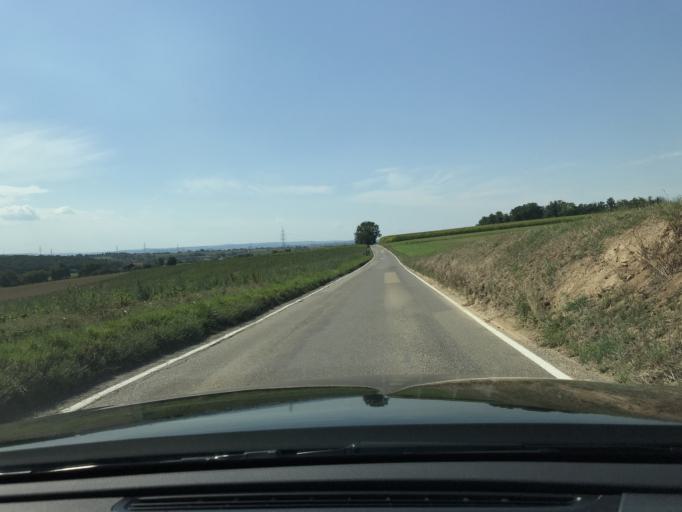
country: DE
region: Baden-Wuerttemberg
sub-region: Regierungsbezirk Stuttgart
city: Affalterbach
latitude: 48.9105
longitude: 9.3140
